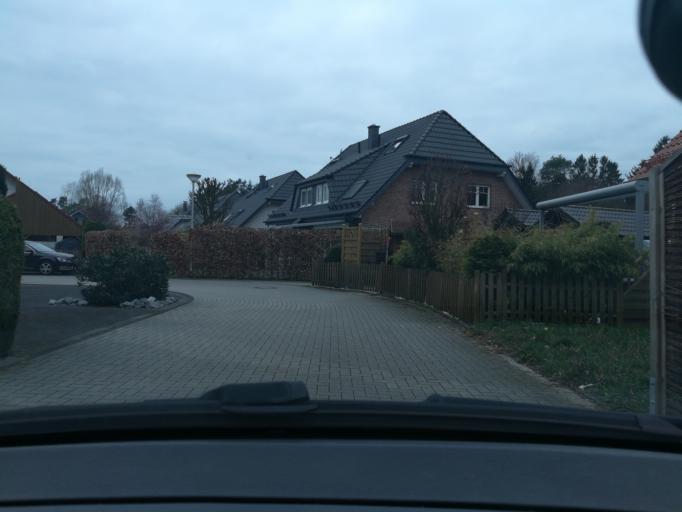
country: DE
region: North Rhine-Westphalia
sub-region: Regierungsbezirk Detmold
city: Oerlinghausen
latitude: 51.9387
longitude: 8.6345
